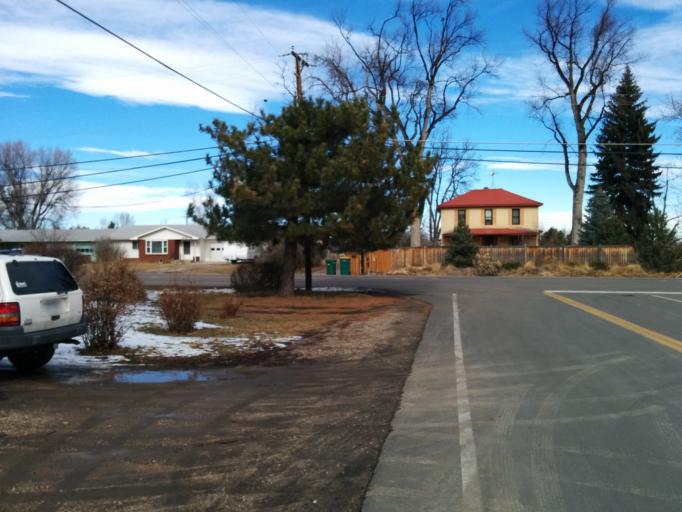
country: US
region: Colorado
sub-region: Larimer County
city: Laporte
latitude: 40.5963
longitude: -105.1259
